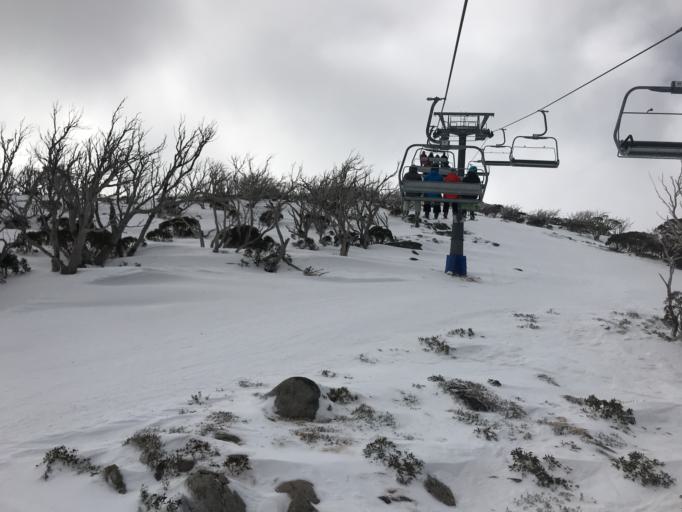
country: AU
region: New South Wales
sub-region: Snowy River
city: Jindabyne
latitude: -36.3835
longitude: 148.3821
